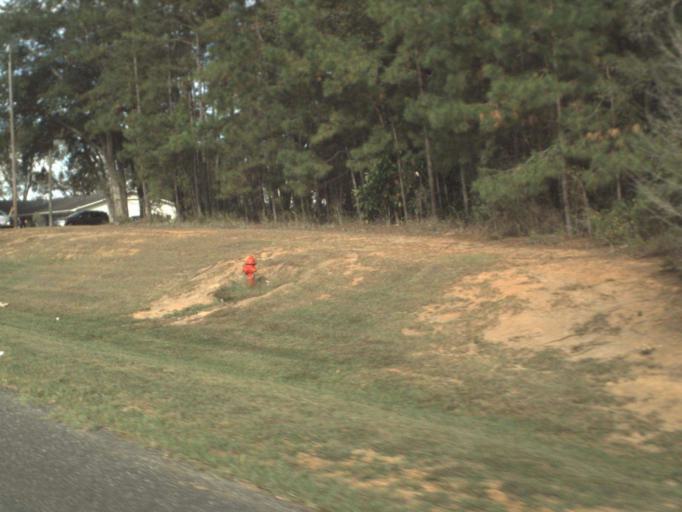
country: US
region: Florida
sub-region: Jefferson County
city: Monticello
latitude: 30.5703
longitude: -83.8698
